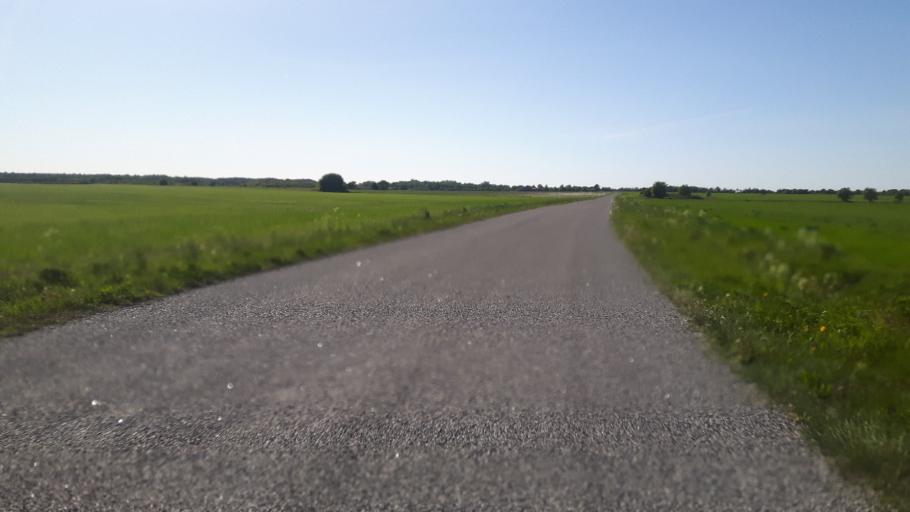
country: EE
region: Ida-Virumaa
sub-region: Kohtla-Jaerve linn
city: Kohtla-Jarve
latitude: 59.4308
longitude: 27.2174
